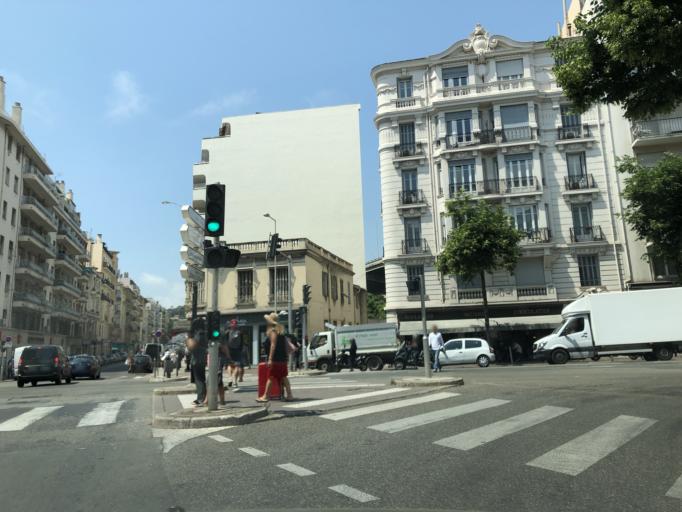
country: FR
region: Provence-Alpes-Cote d'Azur
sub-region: Departement des Alpes-Maritimes
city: Nice
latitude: 43.7018
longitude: 7.2566
